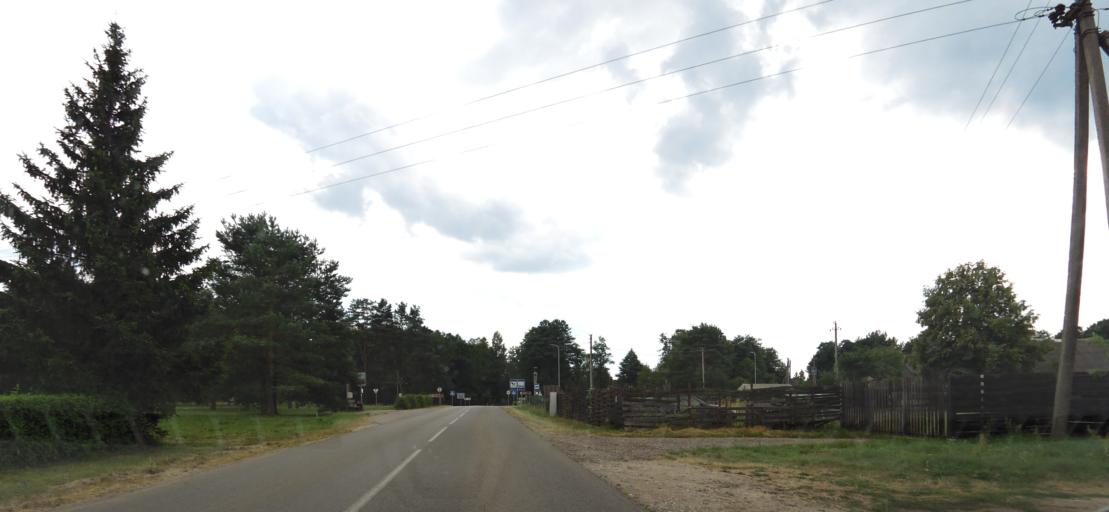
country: LT
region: Alytaus apskritis
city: Druskininkai
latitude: 53.9901
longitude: 24.0431
